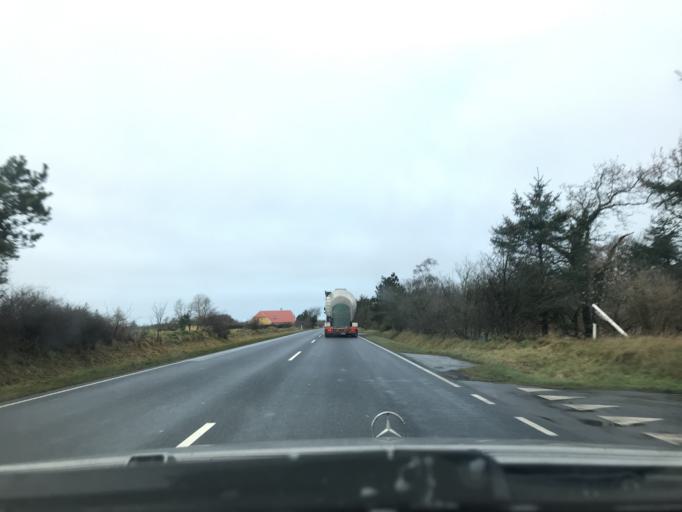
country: DK
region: South Denmark
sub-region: Esbjerg Kommune
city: Ribe
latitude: 55.3049
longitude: 8.8023
